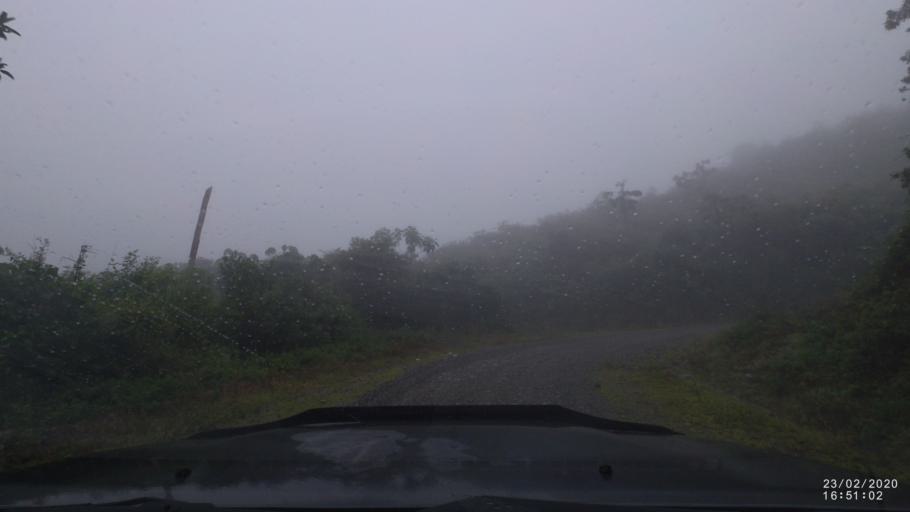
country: BO
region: Cochabamba
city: Colomi
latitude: -17.0916
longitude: -65.9836
